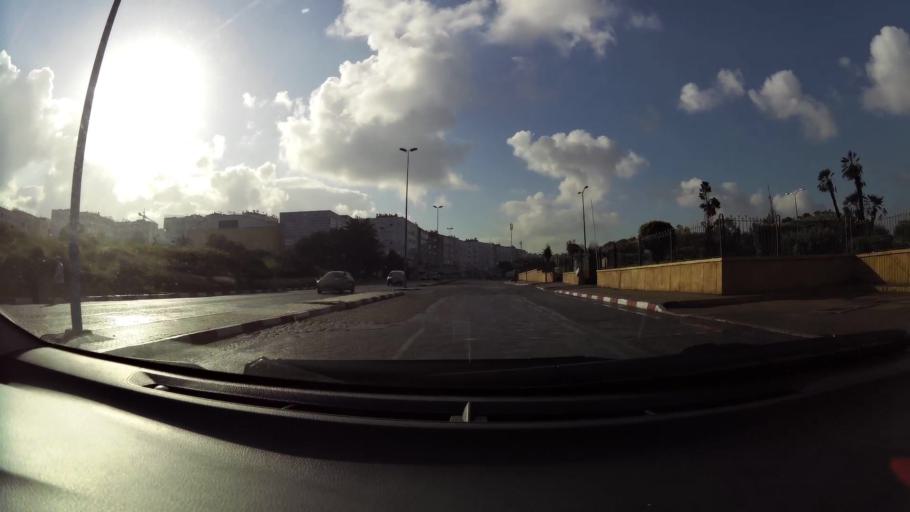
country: MA
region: Grand Casablanca
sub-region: Mediouna
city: Tit Mellil
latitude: 33.6011
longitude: -7.5267
